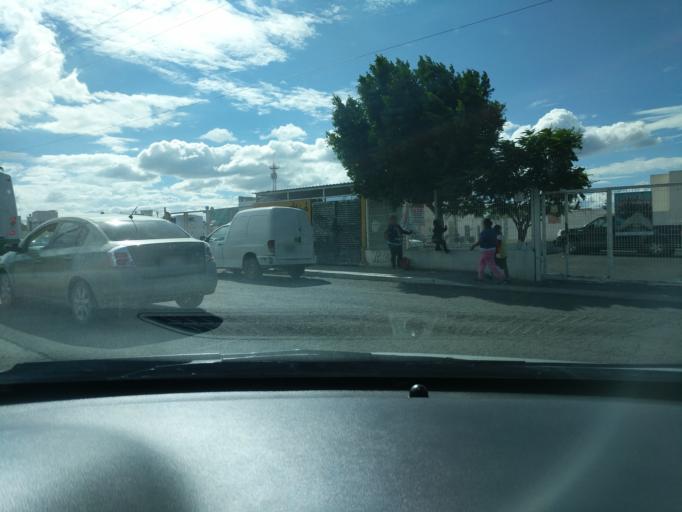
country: MX
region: Queretaro
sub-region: El Marques
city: Paseos del Marques
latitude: 20.6038
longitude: -100.2377
